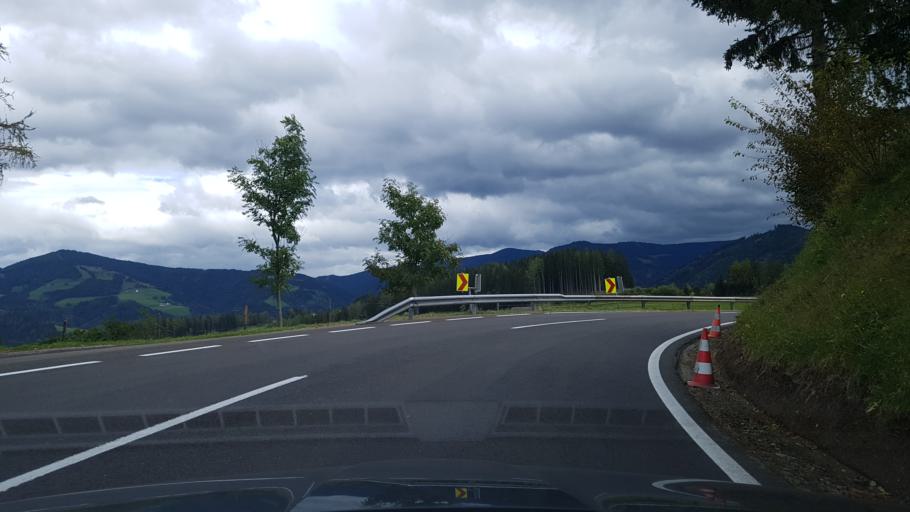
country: AT
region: Styria
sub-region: Politischer Bezirk Murtal
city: Kleinlobming
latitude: 47.1432
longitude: 14.8150
